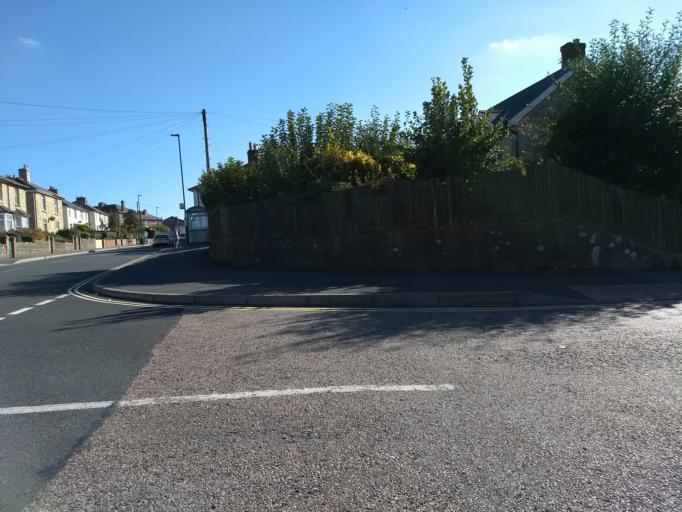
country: GB
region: England
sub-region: Isle of Wight
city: Ventnor
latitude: 50.5988
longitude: -1.2173
